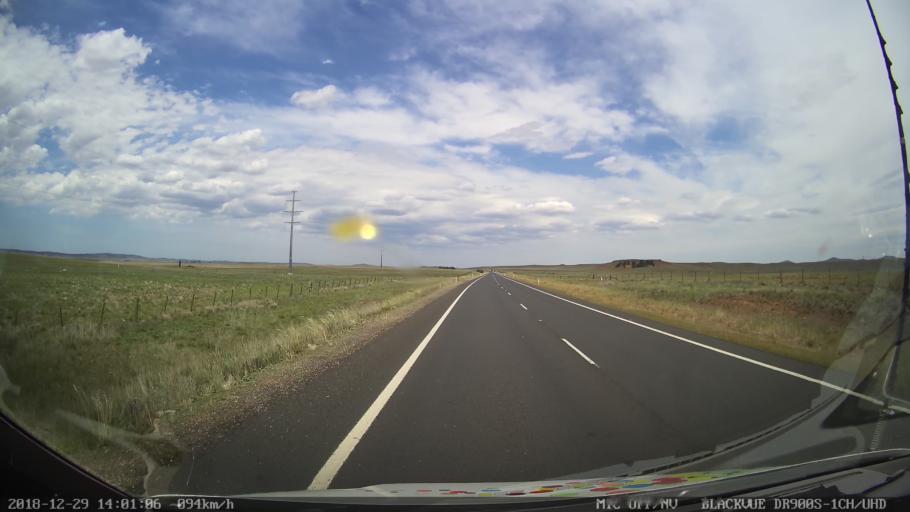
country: AU
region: New South Wales
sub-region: Cooma-Monaro
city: Cooma
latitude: -36.2711
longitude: 149.1660
